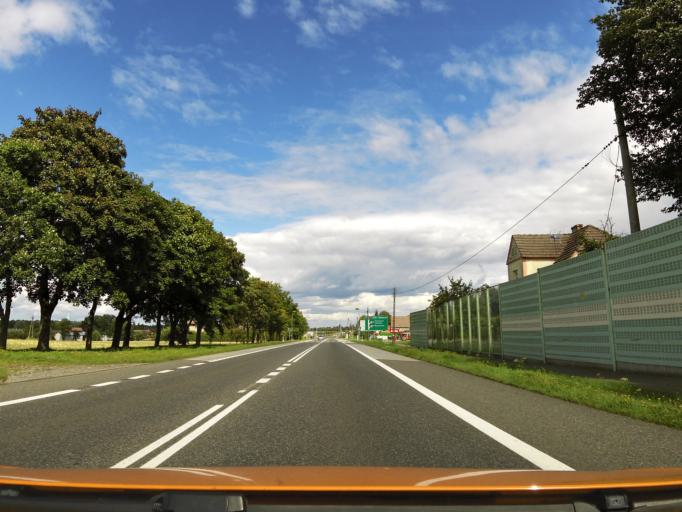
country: PL
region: West Pomeranian Voivodeship
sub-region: Powiat goleniowski
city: Nowogard
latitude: 53.6483
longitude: 15.0666
